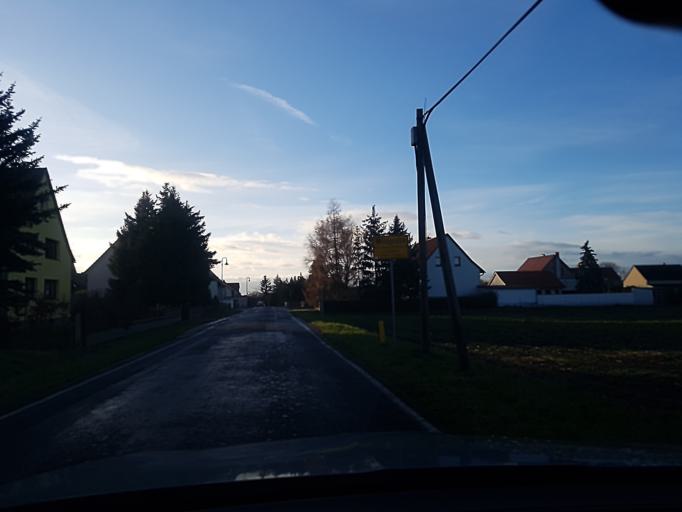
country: DE
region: Brandenburg
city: Schilda
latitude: 51.5878
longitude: 13.3885
